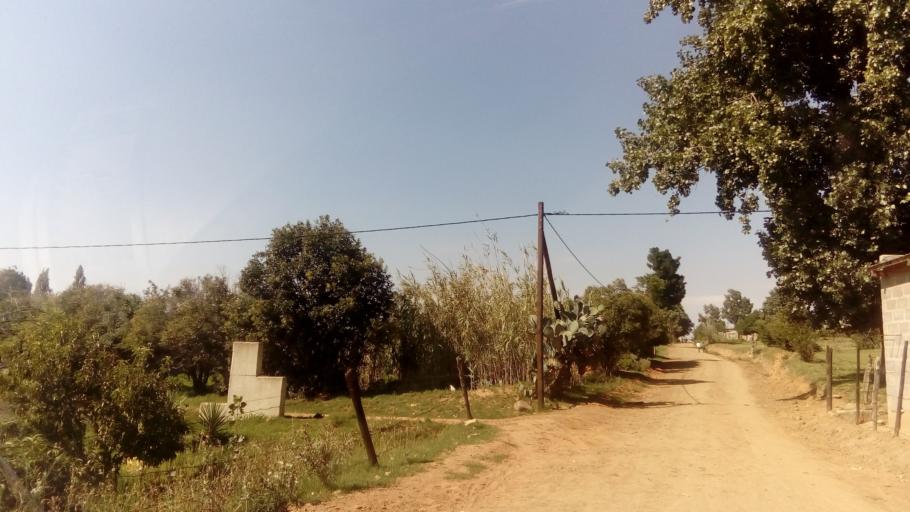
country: LS
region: Berea
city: Teyateyaneng
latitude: -29.1449
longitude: 27.7521
